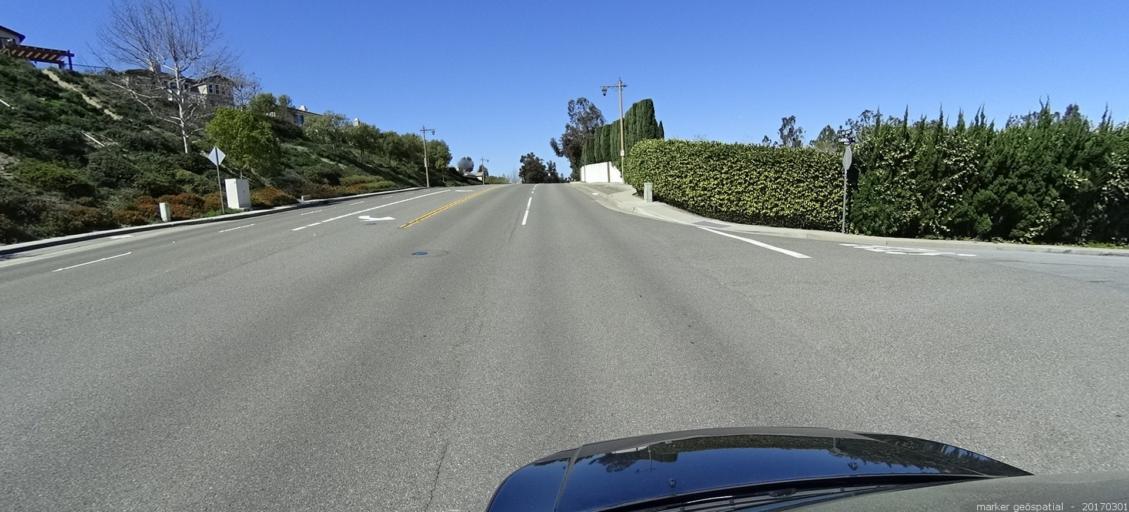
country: US
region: California
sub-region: Orange County
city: Villa Park
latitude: 33.8318
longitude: -117.7613
